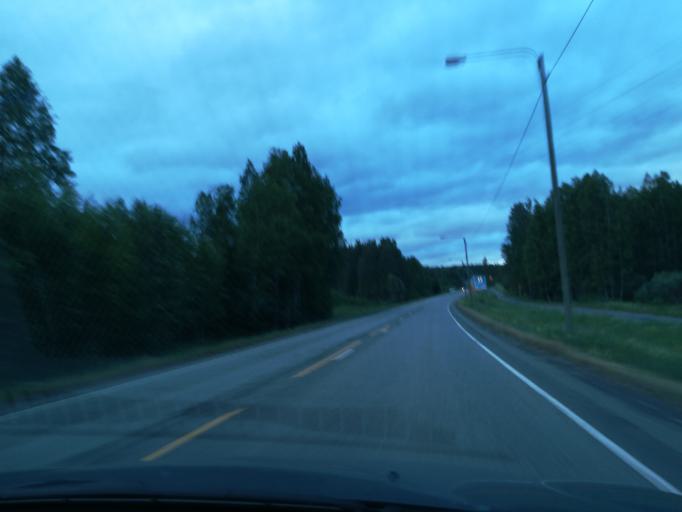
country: FI
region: Southern Savonia
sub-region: Mikkeli
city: Ristiina
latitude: 61.5062
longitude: 27.2380
